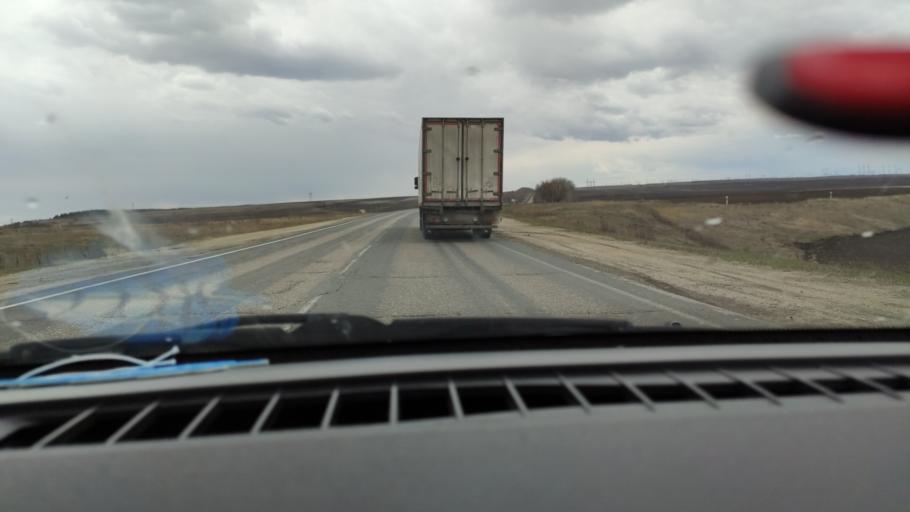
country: RU
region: Saratov
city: Sinodskoye
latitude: 51.9702
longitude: 46.6403
